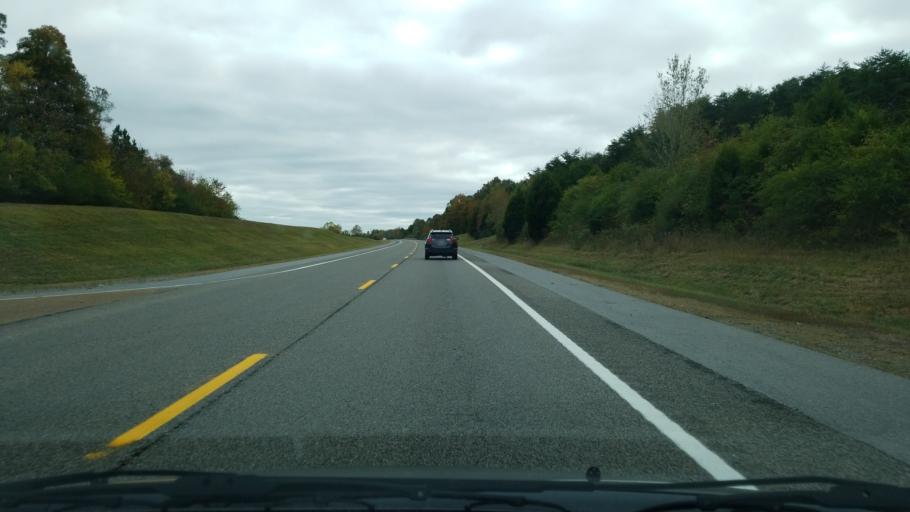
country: US
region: Tennessee
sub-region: Rhea County
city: Graysville
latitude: 35.4266
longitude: -85.0252
